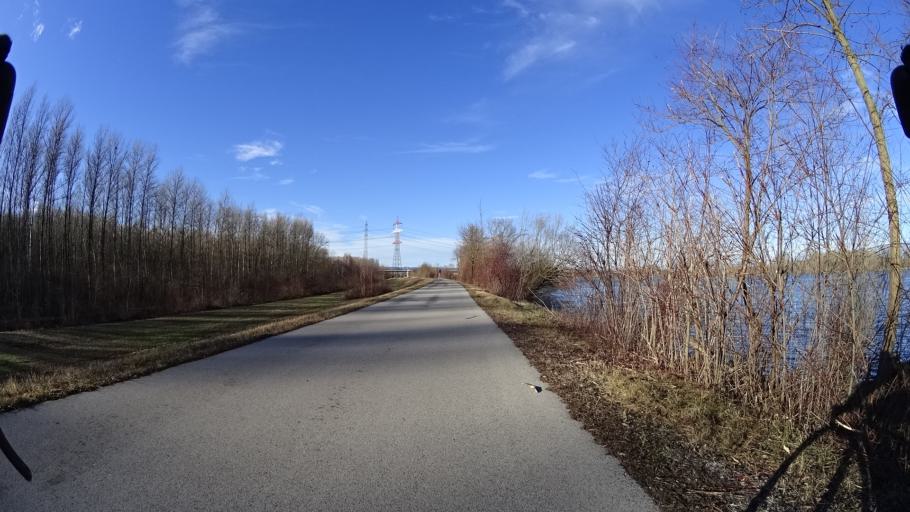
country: AT
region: Lower Austria
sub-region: Politischer Bezirk Sankt Polten
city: Traismauer
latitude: 48.3778
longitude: 15.7296
